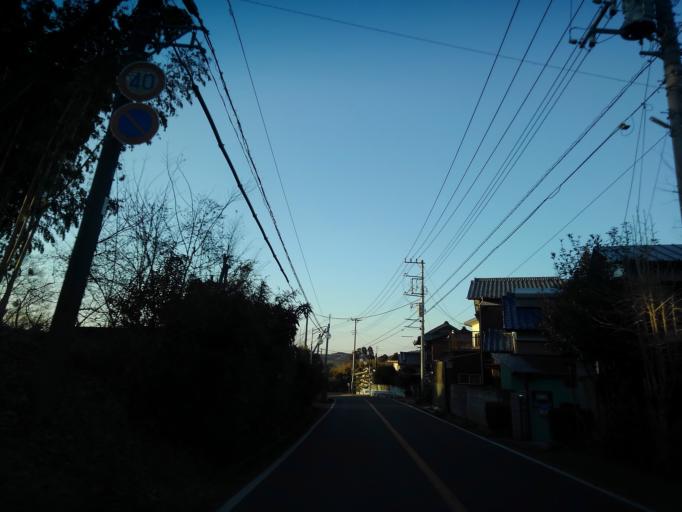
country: JP
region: Chiba
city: Kimitsu
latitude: 35.2978
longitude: 139.9790
